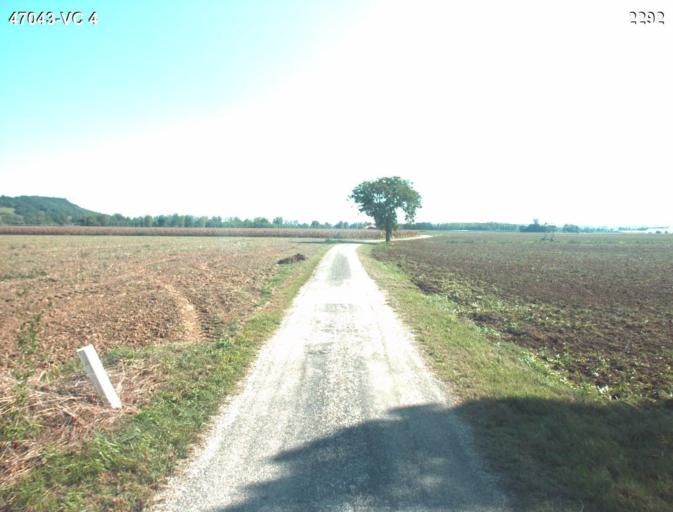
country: FR
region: Aquitaine
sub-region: Departement du Lot-et-Garonne
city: Buzet-sur-Baise
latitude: 44.2707
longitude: 0.3260
